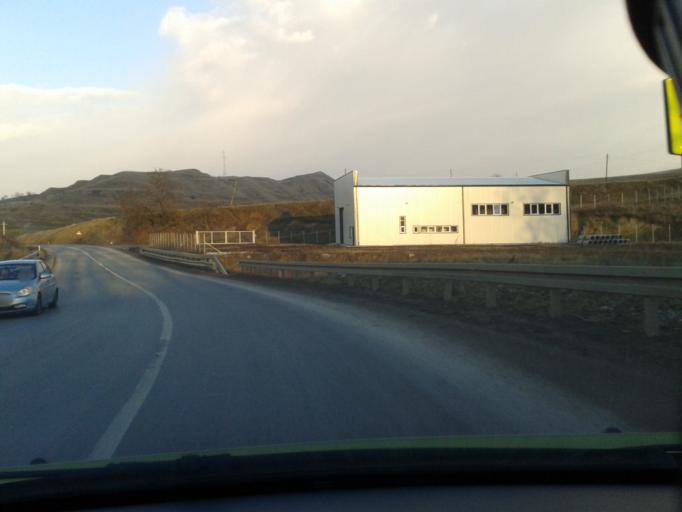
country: RO
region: Sibiu
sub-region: Comuna Tarnava
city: Tarnava
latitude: 46.1272
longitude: 24.2958
